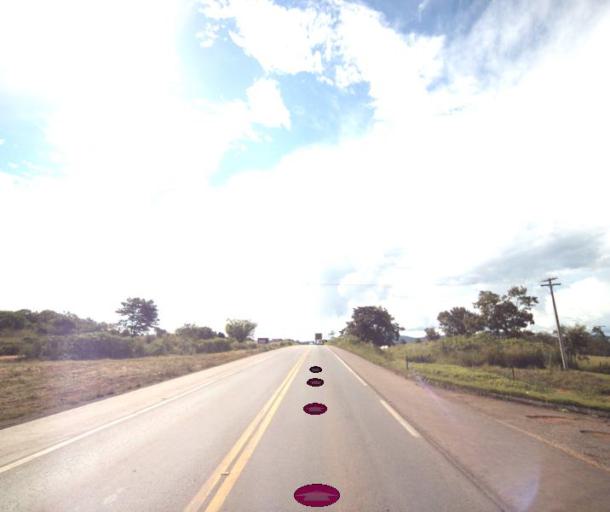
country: BR
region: Goias
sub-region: Jaragua
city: Jaragua
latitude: -15.7409
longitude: -49.3209
